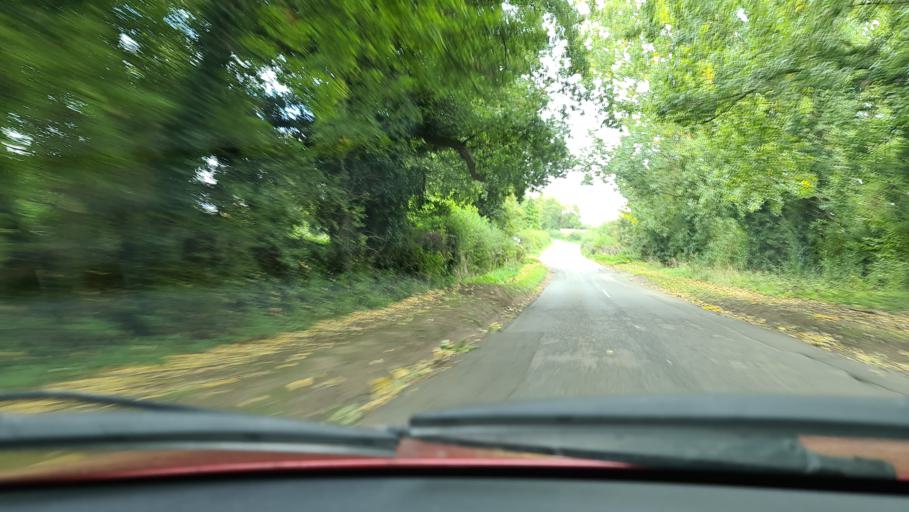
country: GB
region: England
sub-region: Oxfordshire
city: Adderbury
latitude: 52.0179
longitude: -1.2732
